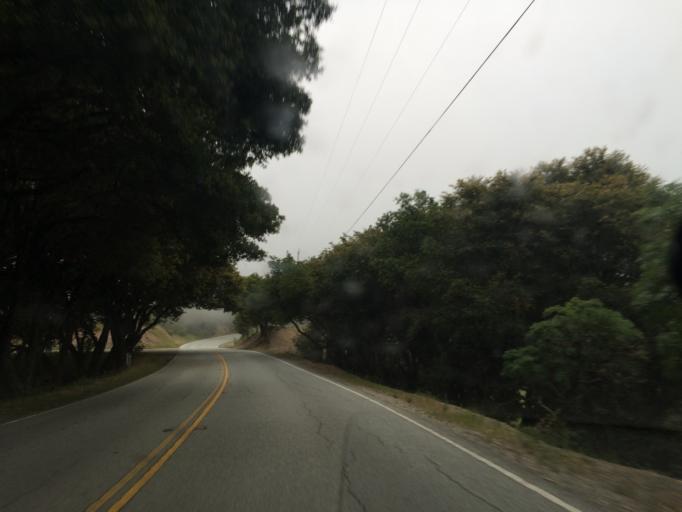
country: US
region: California
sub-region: Santa Clara County
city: Loyola
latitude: 37.2832
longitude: -122.1512
